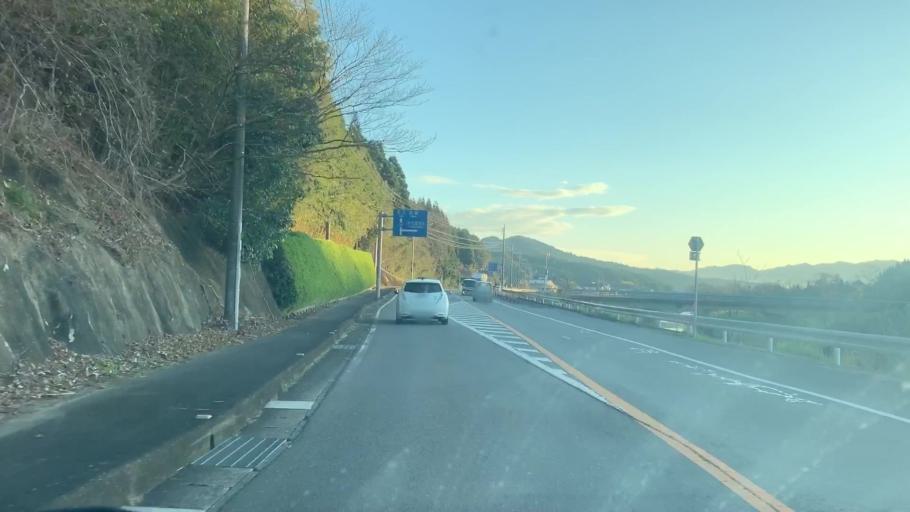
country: JP
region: Saga Prefecture
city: Imaricho-ko
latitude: 33.2721
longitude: 129.9647
